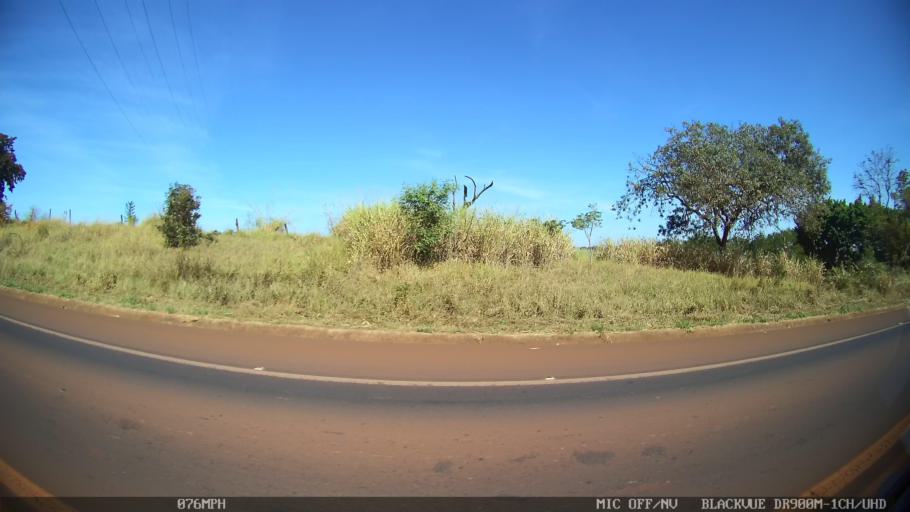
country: BR
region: Sao Paulo
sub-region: Sao Joaquim Da Barra
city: Sao Joaquim da Barra
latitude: -20.5391
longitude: -47.8193
